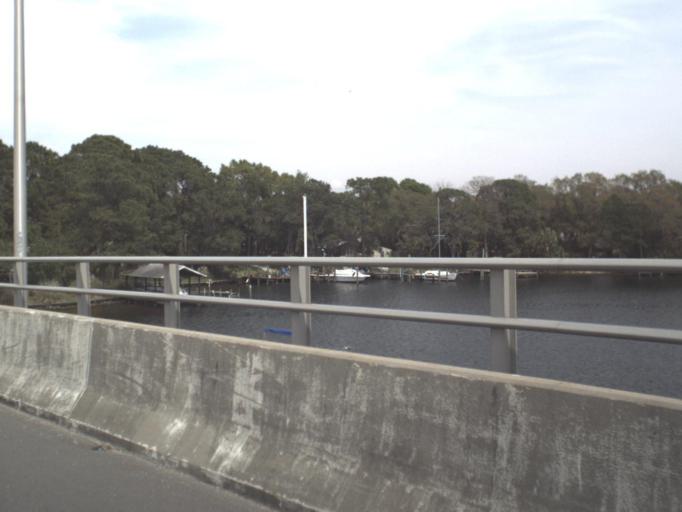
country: US
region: Florida
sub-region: Okaloosa County
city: Ocean City
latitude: 30.4269
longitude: -86.6075
